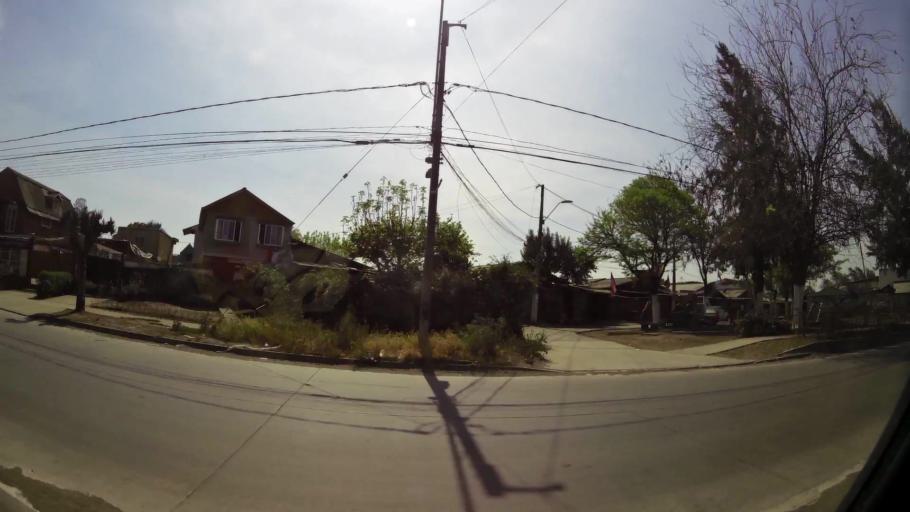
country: CL
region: Santiago Metropolitan
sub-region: Provincia de Santiago
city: Lo Prado
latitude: -33.4277
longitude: -70.7550
